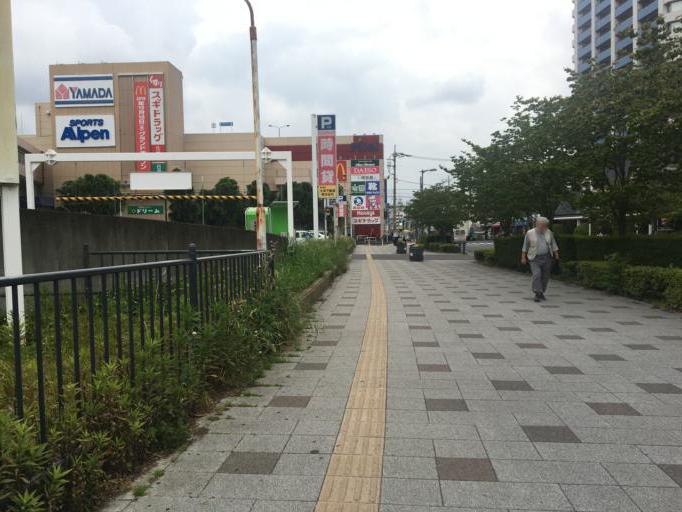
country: JP
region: Saitama
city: Kawaguchi
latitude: 35.8014
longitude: 139.7289
